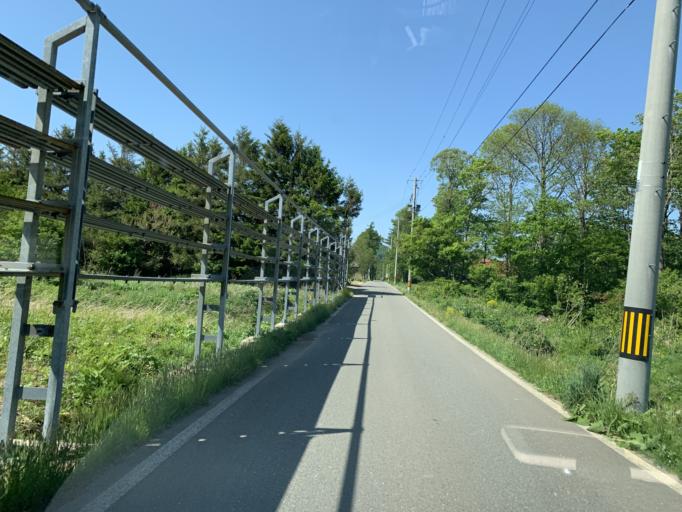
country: JP
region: Iwate
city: Shizukuishi
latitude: 39.5563
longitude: 140.8309
